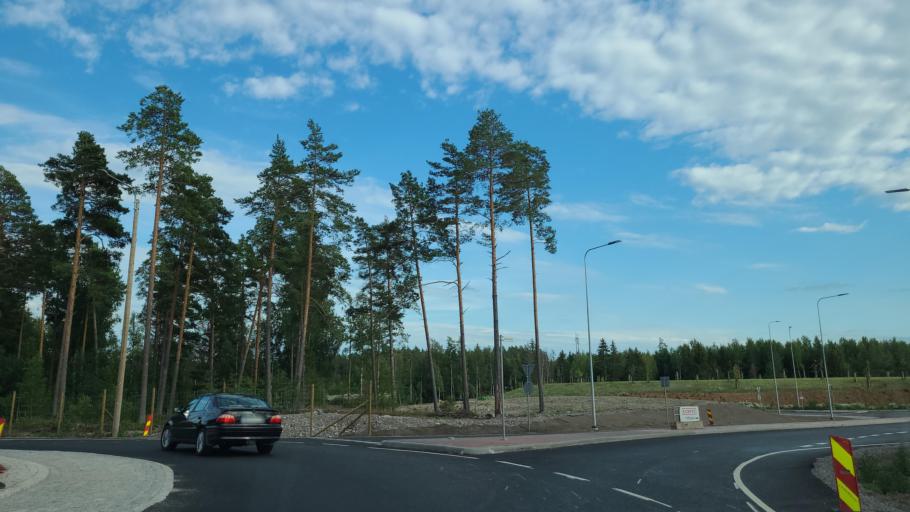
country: FI
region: Varsinais-Suomi
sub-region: Turku
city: Naantali
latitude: 60.4568
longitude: 21.9904
